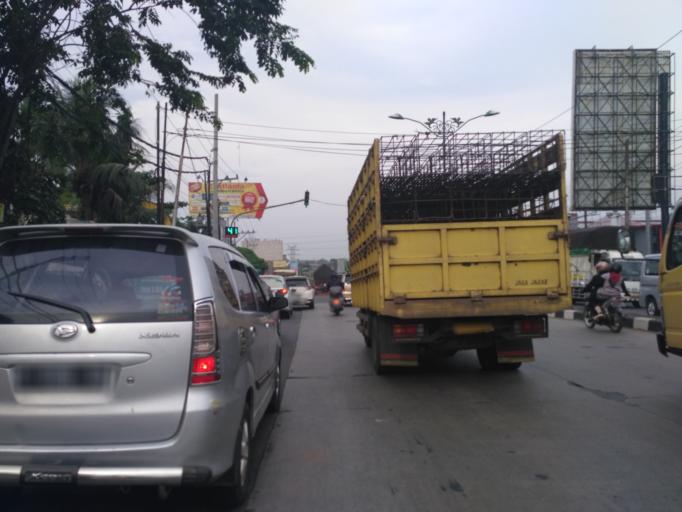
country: ID
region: Central Java
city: Semarang
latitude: -6.9866
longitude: 110.3601
